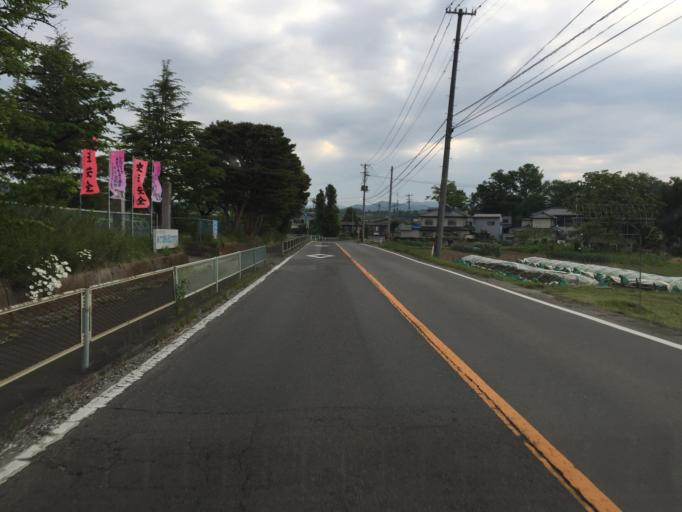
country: JP
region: Fukushima
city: Yanagawamachi-saiwaicho
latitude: 37.8769
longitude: 140.5925
